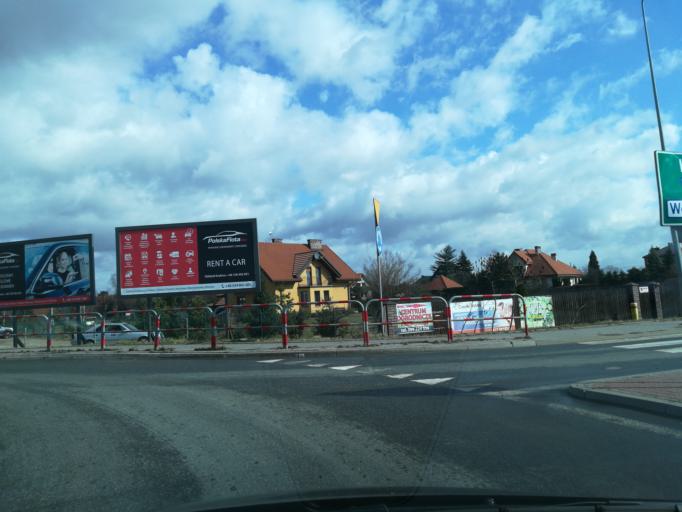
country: PL
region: Lesser Poland Voivodeship
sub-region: Powiat krakowski
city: Kryspinow
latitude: 50.0622
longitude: 19.8044
